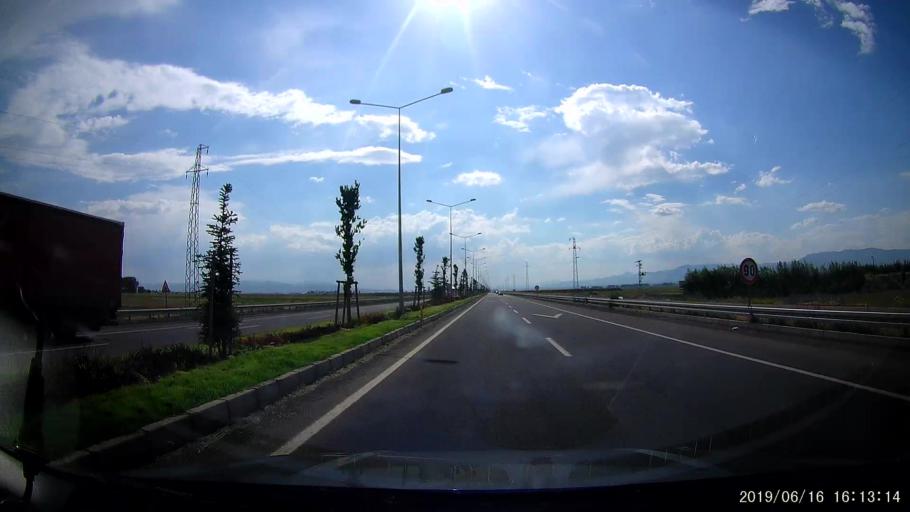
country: TR
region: Erzurum
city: Erzurum
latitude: 39.9594
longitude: 41.2759
